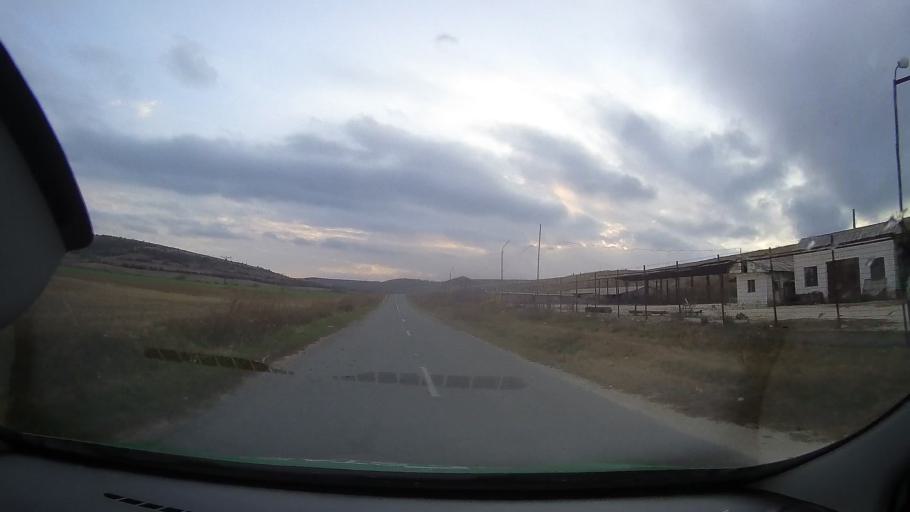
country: RO
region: Constanta
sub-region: Comuna Dobromir
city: Dobromir
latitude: 44.0242
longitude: 27.7921
